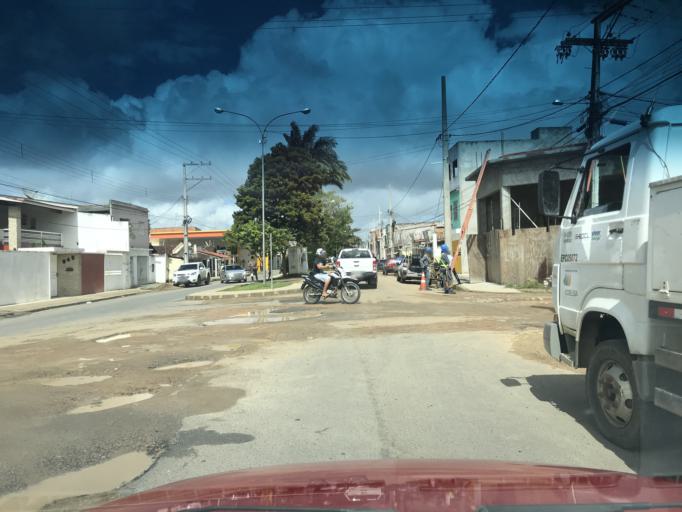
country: BR
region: Bahia
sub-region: Santo Antonio De Jesus
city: Santo Antonio de Jesus
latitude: -12.9745
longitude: -39.2739
